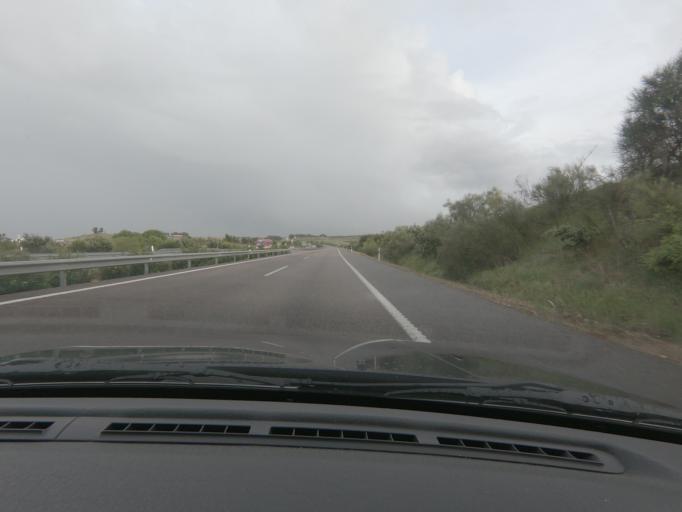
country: ES
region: Extremadura
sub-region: Provincia de Badajoz
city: Badajoz
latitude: 38.8826
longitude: -6.8897
